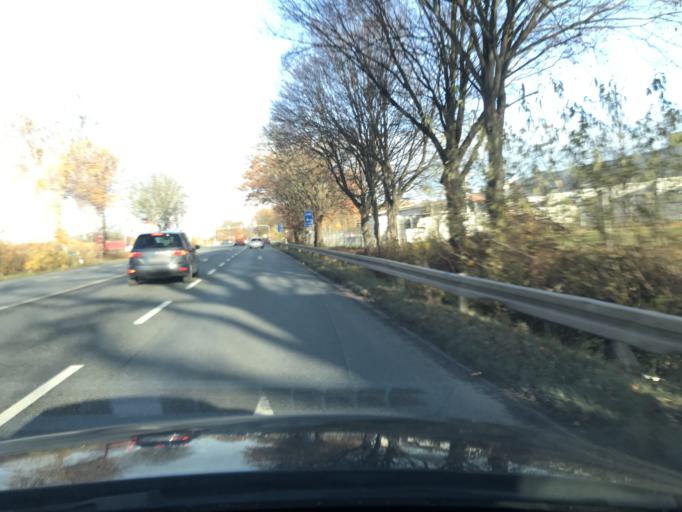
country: DE
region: North Rhine-Westphalia
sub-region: Regierungsbezirk Arnsberg
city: Hamm
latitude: 51.6269
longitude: 7.8471
